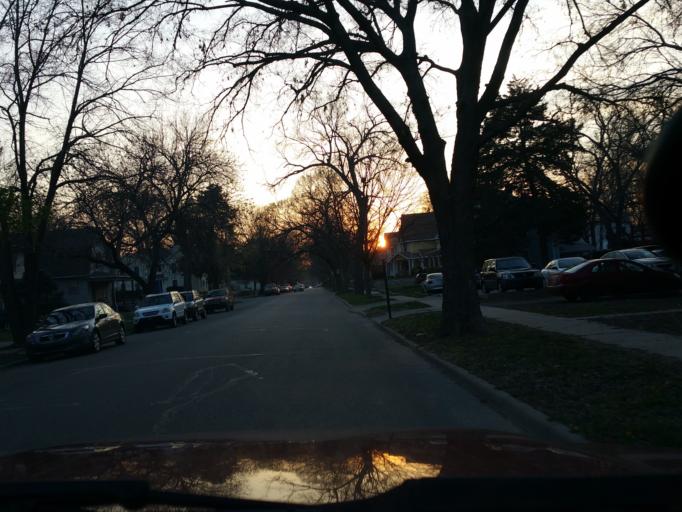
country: US
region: Kansas
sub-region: Riley County
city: Manhattan
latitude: 39.1837
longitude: -96.5688
